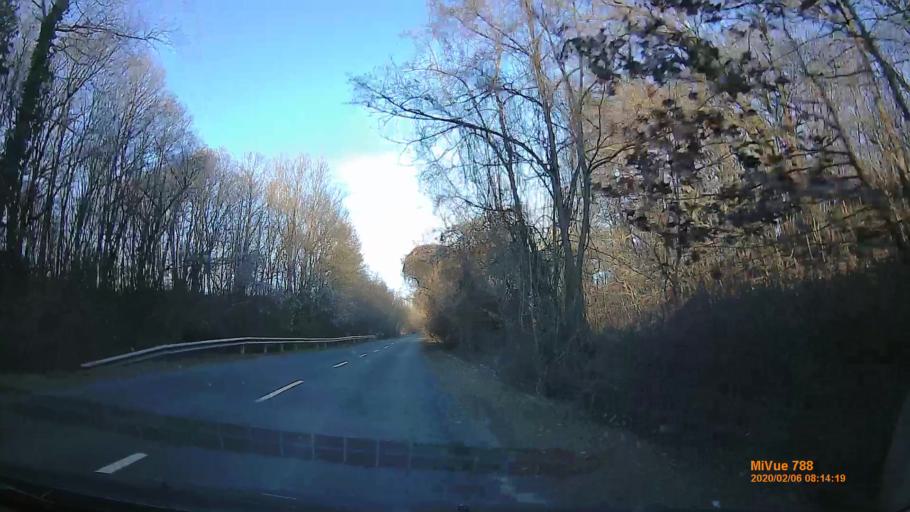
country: HU
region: Fejer
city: Szarliget
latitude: 47.5227
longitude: 18.5120
